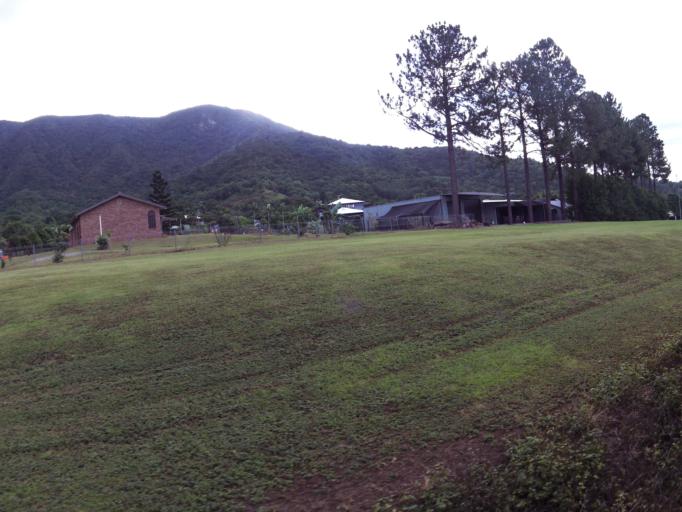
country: AU
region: Queensland
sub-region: Cairns
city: Redlynch
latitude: -16.9025
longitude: 145.6921
